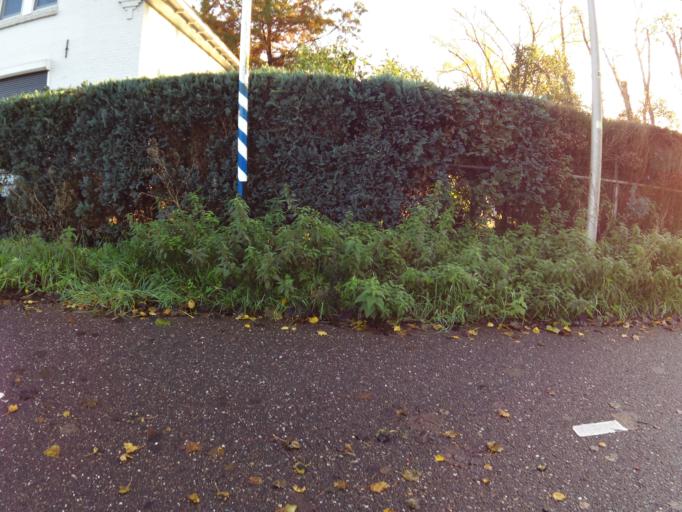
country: NL
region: North Brabant
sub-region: Gemeente Waalwijk
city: Waalwijk
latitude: 51.6915
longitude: 5.1145
